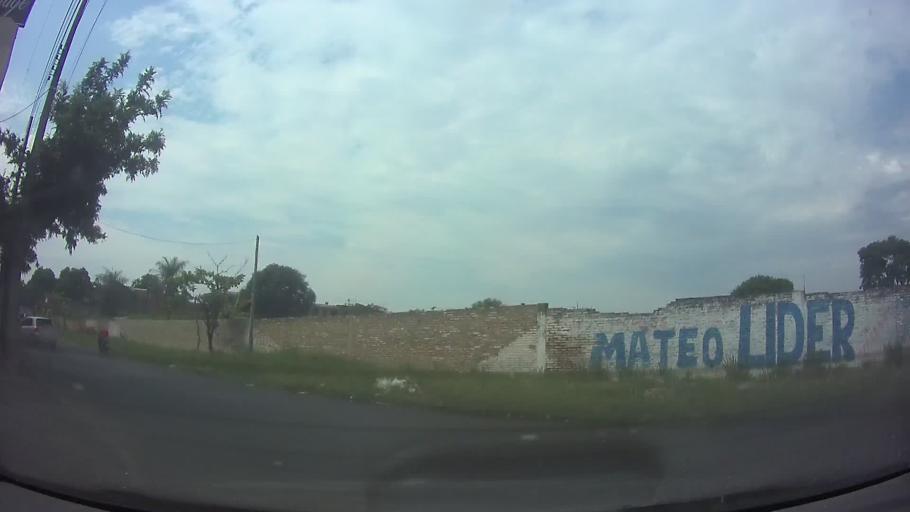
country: PY
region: Central
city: Fernando de la Mora
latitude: -25.3035
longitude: -57.5429
